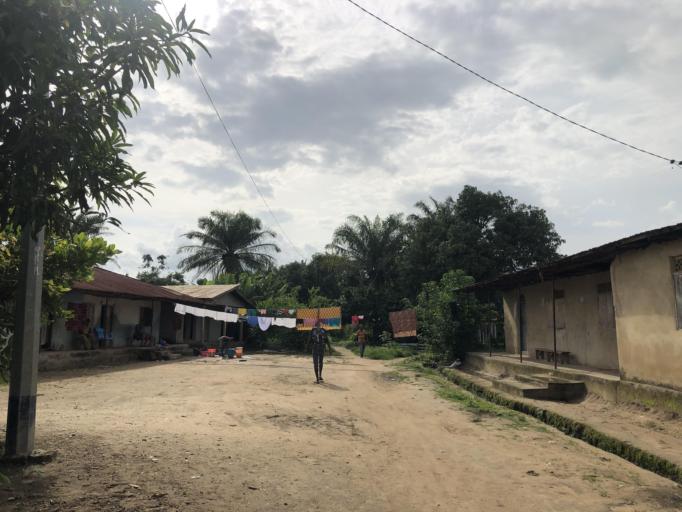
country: SL
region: Northern Province
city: Bumbuna
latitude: 9.0469
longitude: -11.7510
